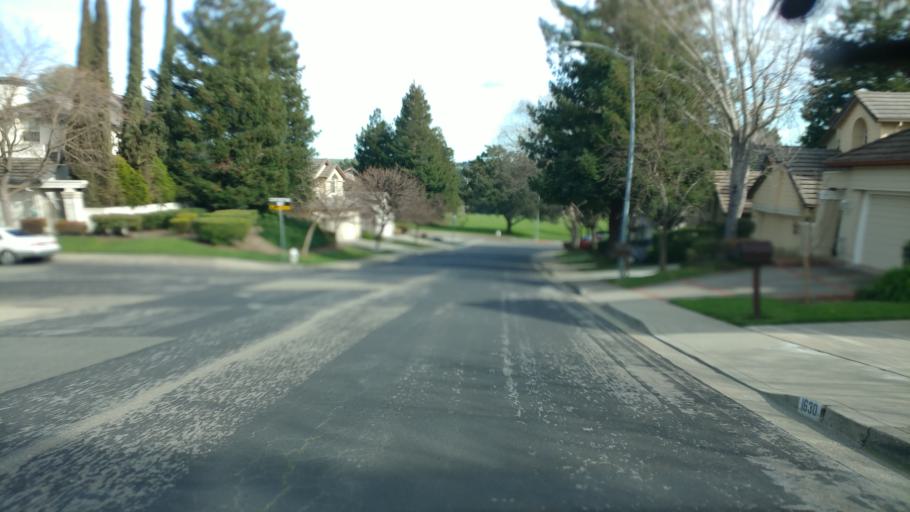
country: US
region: California
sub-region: Contra Costa County
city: San Ramon
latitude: 37.7916
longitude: -121.9860
